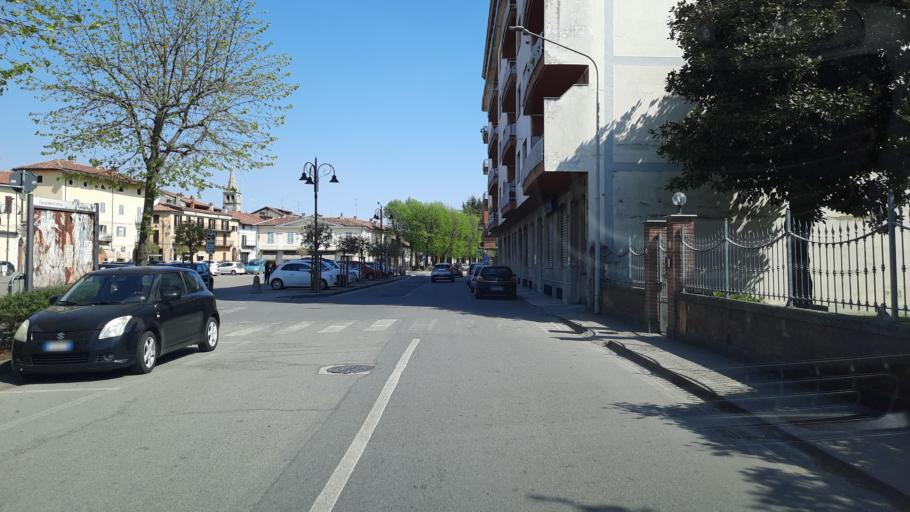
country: IT
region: Piedmont
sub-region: Provincia di Vercelli
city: Crescentino
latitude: 45.1906
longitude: 8.1009
